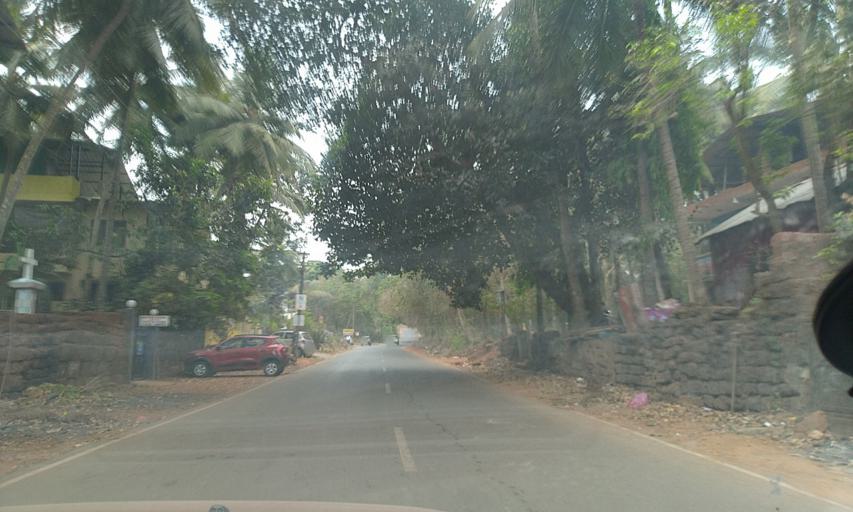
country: IN
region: Goa
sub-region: North Goa
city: Jua
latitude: 15.4967
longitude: 73.9126
